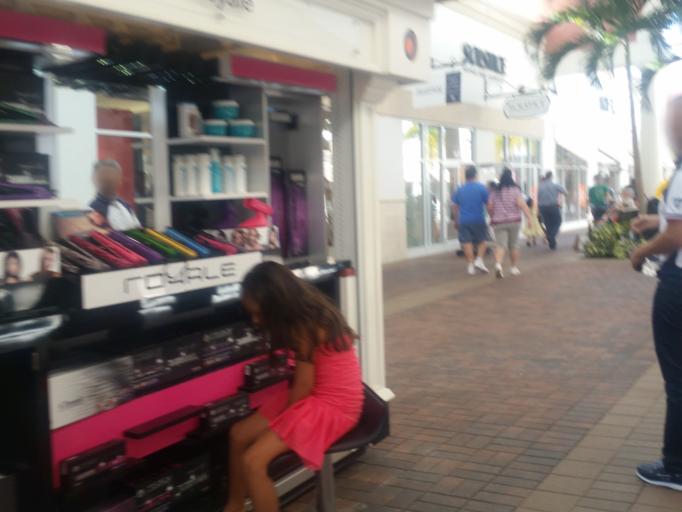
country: US
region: Florida
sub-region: Orange County
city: Tangelo Park
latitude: 28.4737
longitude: -81.4528
